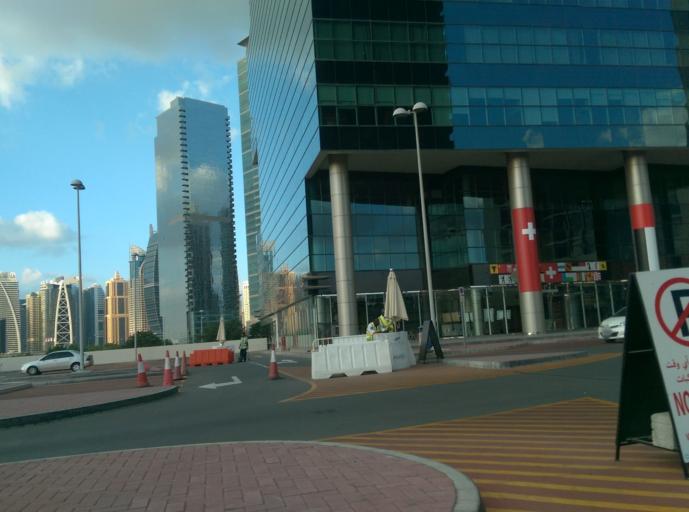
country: AE
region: Dubai
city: Dubai
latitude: 25.0778
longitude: 55.1535
